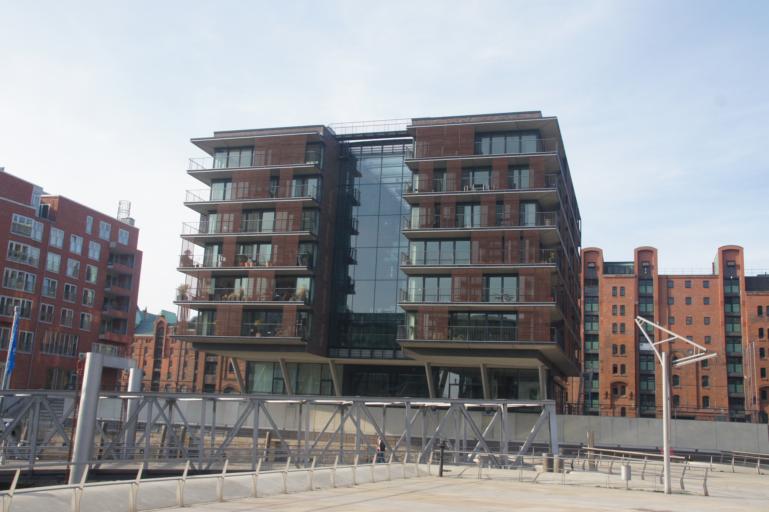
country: DE
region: Hamburg
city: Altstadt
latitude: 53.5422
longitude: 9.9925
